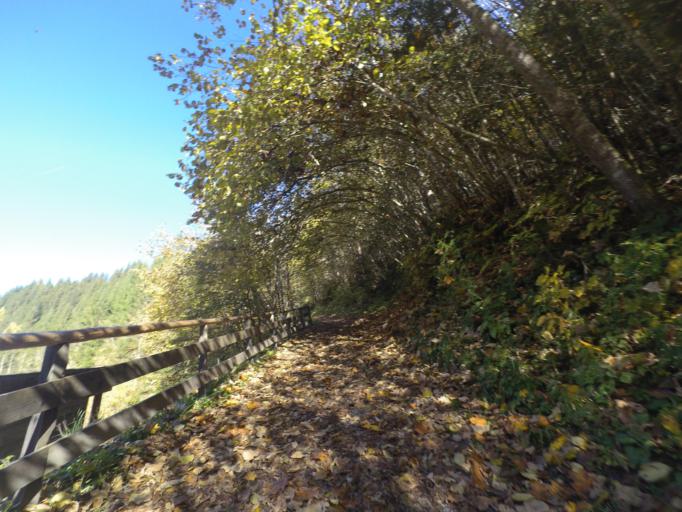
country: AT
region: Salzburg
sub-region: Politischer Bezirk Sankt Johann im Pongau
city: Sankt Johann im Pongau
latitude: 47.3164
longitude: 13.1924
